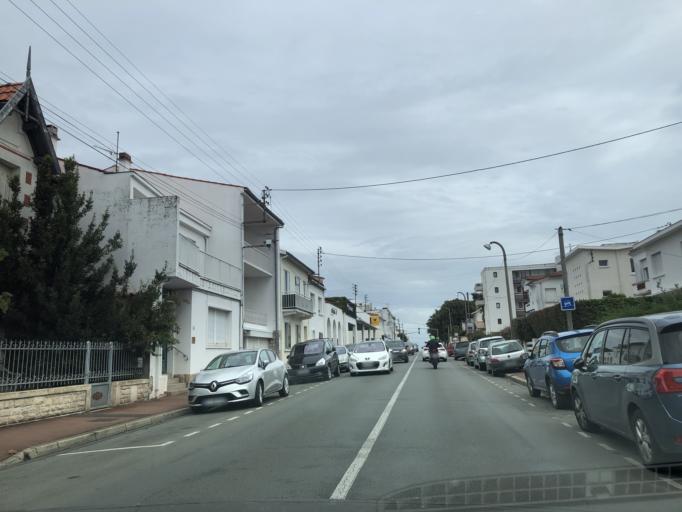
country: FR
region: Poitou-Charentes
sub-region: Departement de la Charente-Maritime
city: Royan
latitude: 45.6225
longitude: -1.0408
